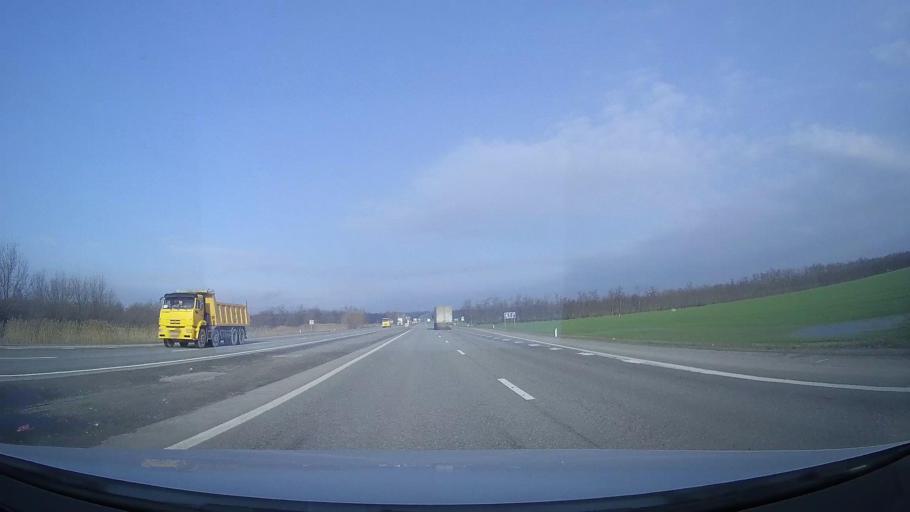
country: RU
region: Rostov
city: Grushevskaya
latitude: 47.4705
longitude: 39.9722
